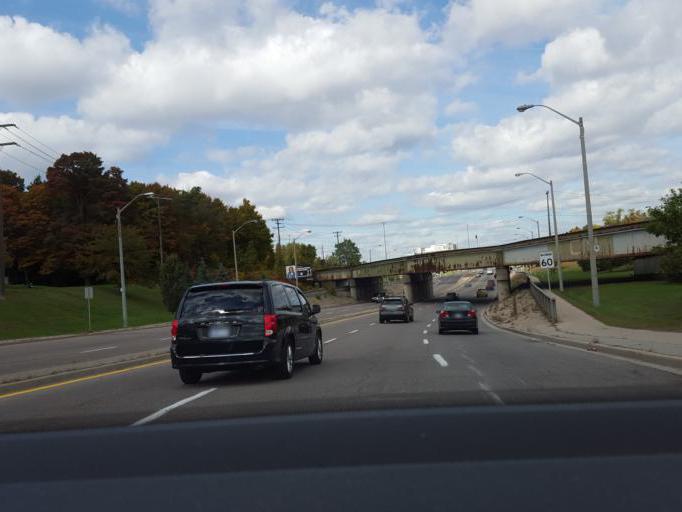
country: CA
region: Ontario
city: Willowdale
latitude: 43.7609
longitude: -79.3617
